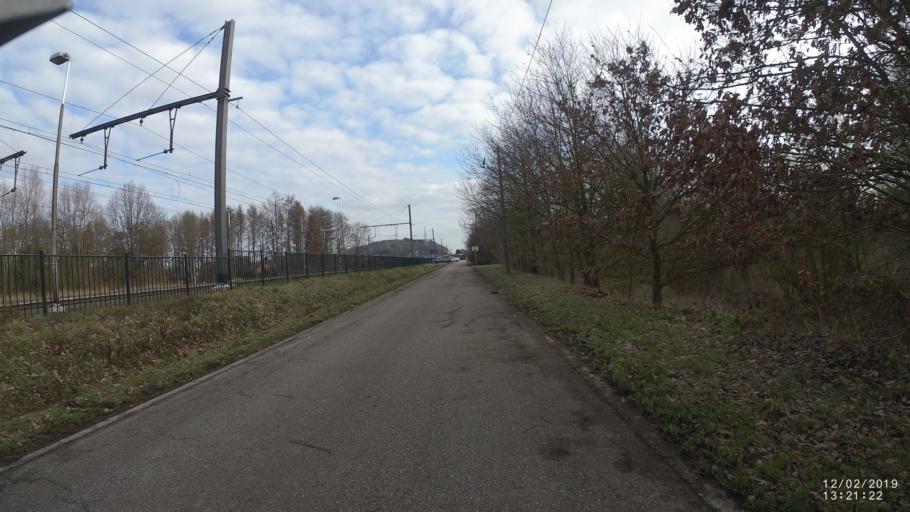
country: BE
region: Flanders
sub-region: Provincie Vlaams-Brabant
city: Scherpenheuvel-Zichem
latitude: 51.0098
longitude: 4.9429
